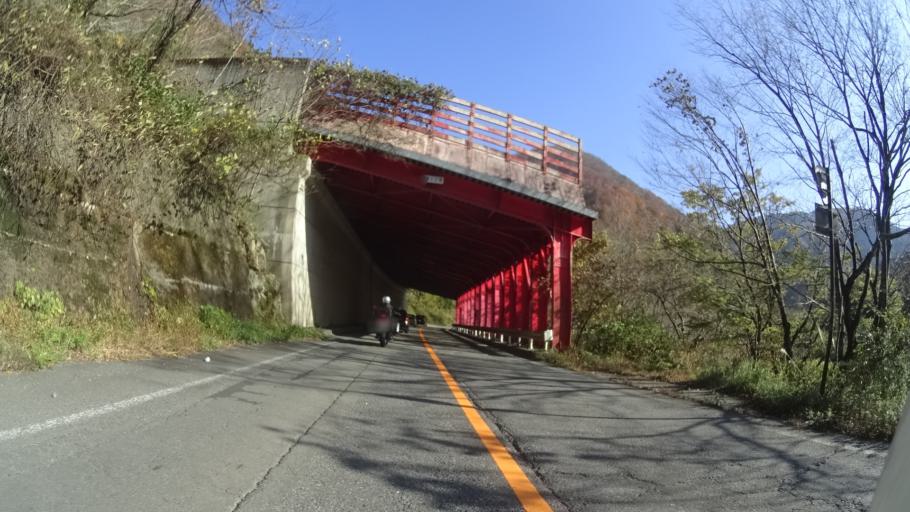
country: JP
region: Fukui
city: Ono
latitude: 35.9510
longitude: 136.6381
